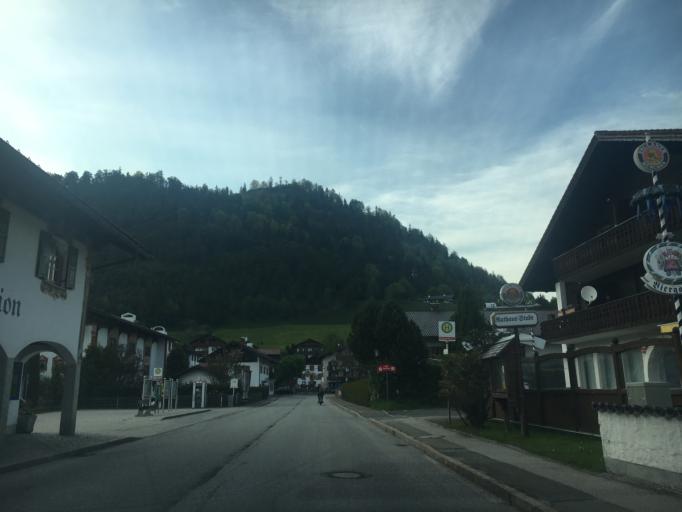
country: DE
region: Bavaria
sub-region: Upper Bavaria
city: Wallgau
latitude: 47.5199
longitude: 11.2824
